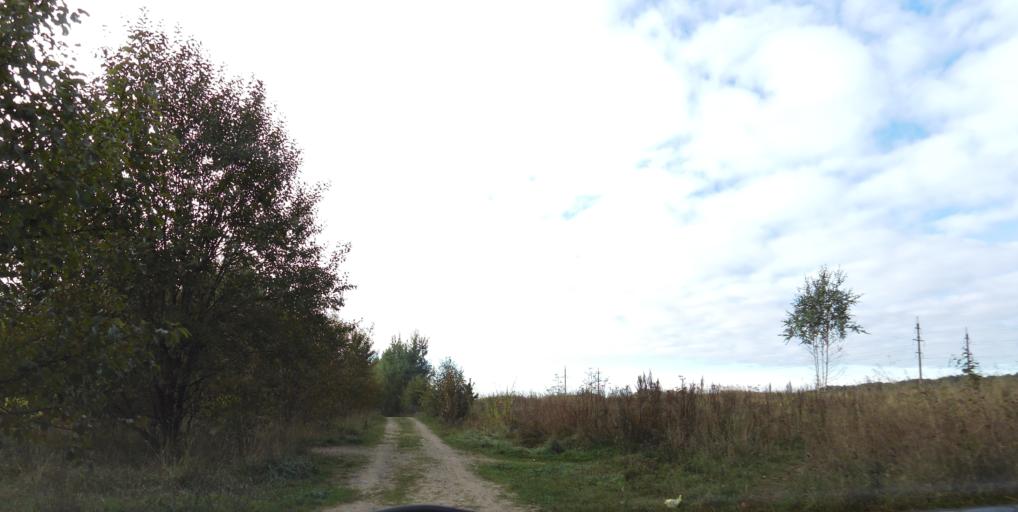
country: LT
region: Vilnius County
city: Justiniskes
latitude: 54.7162
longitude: 25.2098
